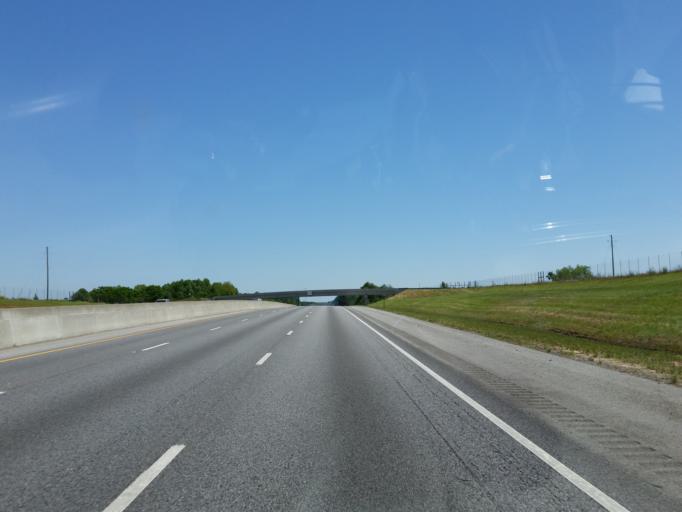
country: US
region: Georgia
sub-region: Turner County
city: Ashburn
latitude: 31.6487
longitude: -83.5943
